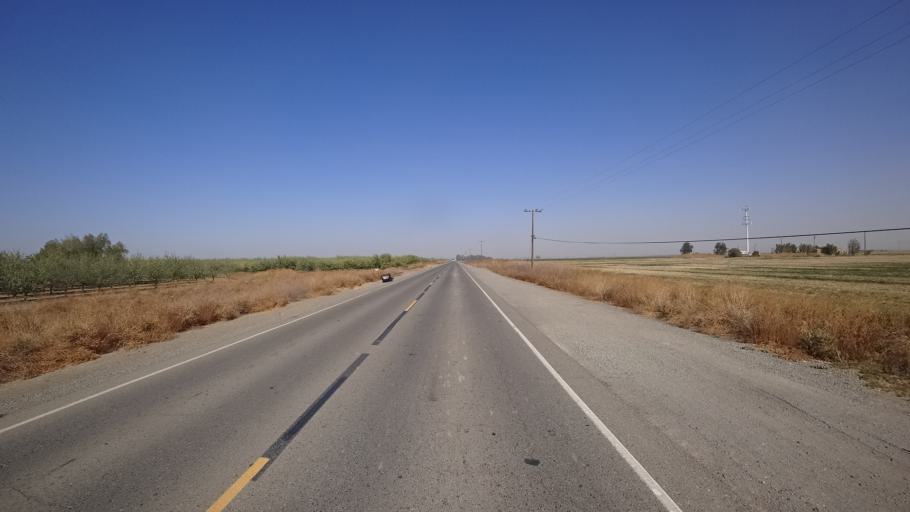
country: US
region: California
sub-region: Yolo County
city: Davis
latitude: 38.5595
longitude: -121.6756
